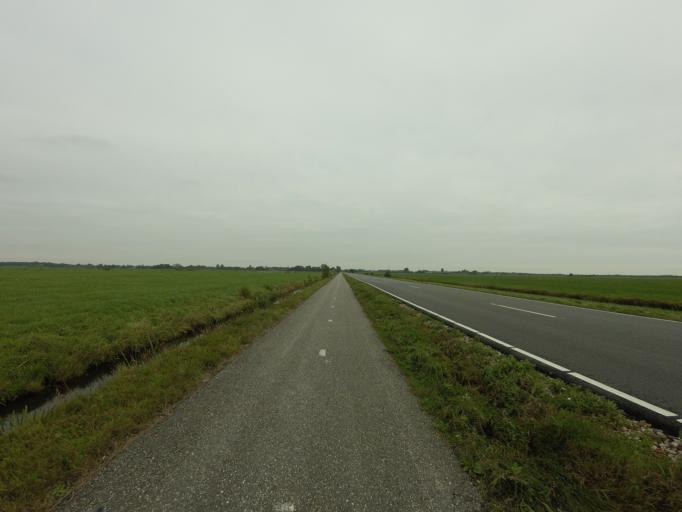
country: NL
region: Utrecht
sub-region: Gemeente Woerden
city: Woerden
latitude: 52.1387
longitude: 4.8616
